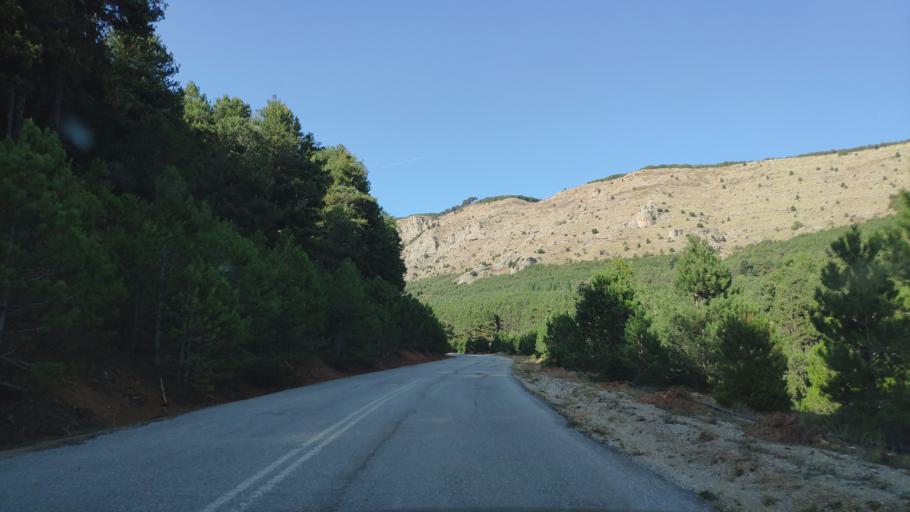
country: GR
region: West Greece
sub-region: Nomos Achaias
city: Aiyira
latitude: 38.0286
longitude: 22.4034
